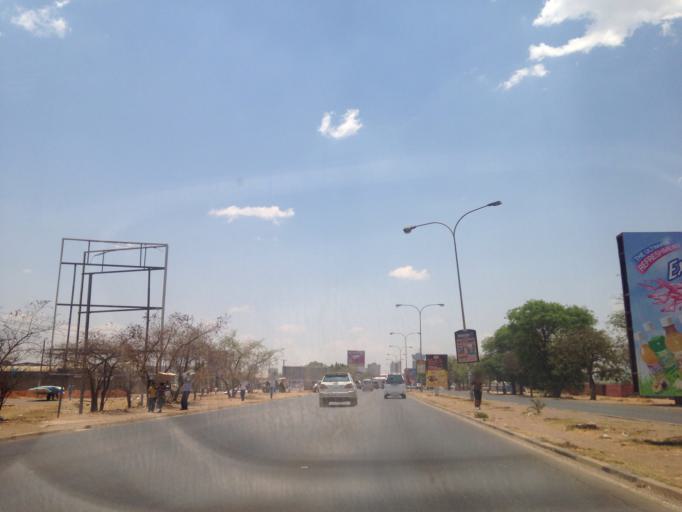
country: ZM
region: Lusaka
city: Lusaka
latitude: -15.4384
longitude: 28.2757
